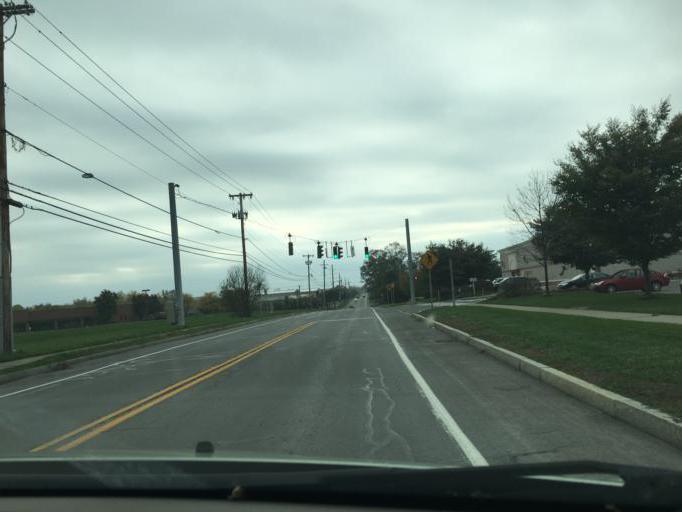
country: US
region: New York
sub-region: Ontario County
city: Canandaigua
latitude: 42.9043
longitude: -77.2952
